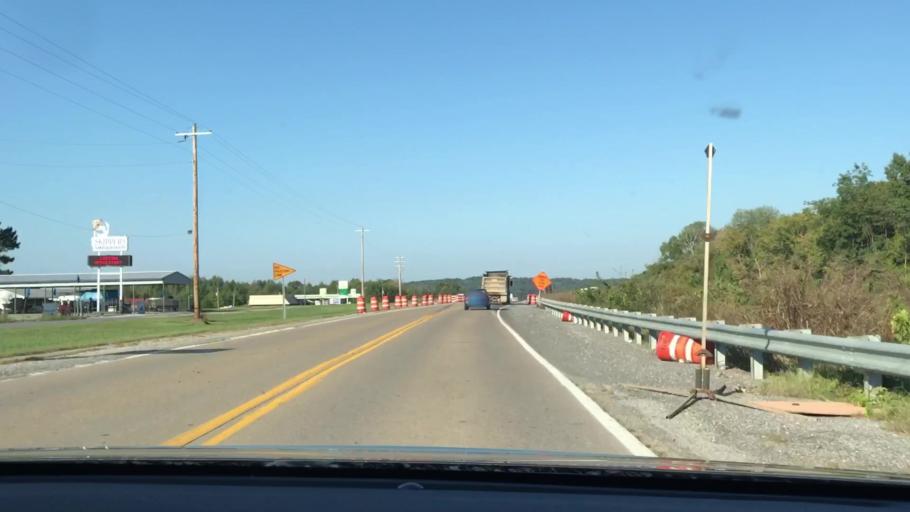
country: US
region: Kentucky
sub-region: Trigg County
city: Cadiz
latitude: 36.7983
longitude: -87.9647
